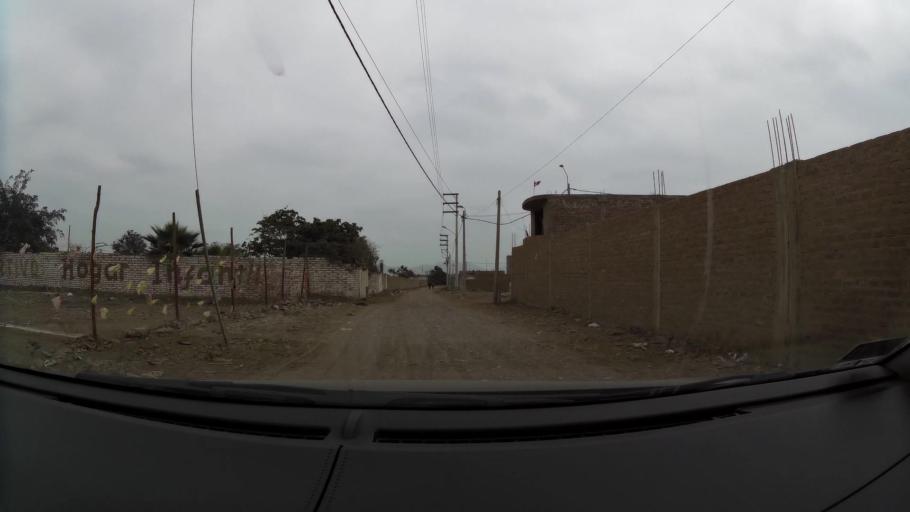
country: PE
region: Lima
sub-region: Provincia de Huaral
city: Huaral
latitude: -11.4858
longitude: -77.2086
